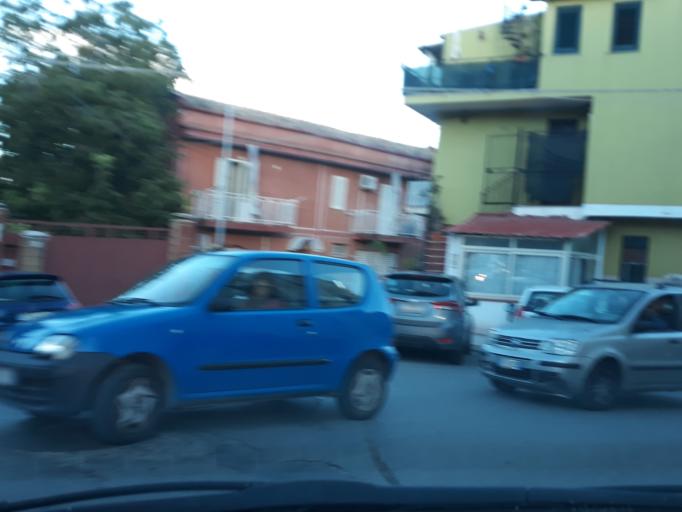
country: IT
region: Sicily
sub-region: Palermo
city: Monreale
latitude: 38.0748
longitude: 13.3030
